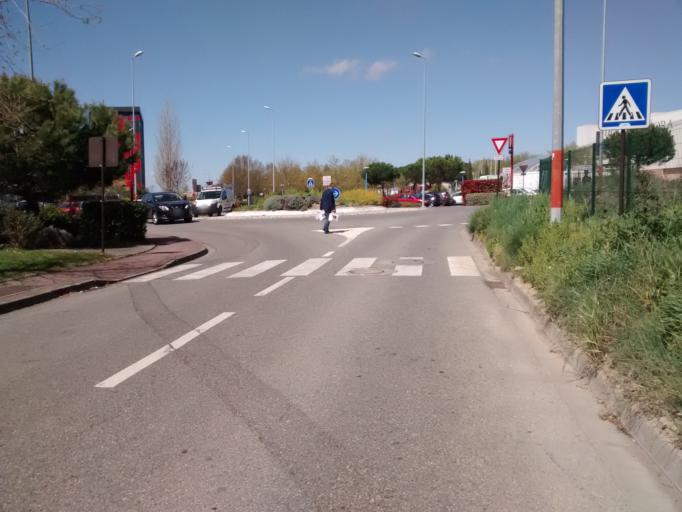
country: FR
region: Midi-Pyrenees
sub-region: Departement de la Haute-Garonne
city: Labege
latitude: 43.5405
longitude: 1.5145
